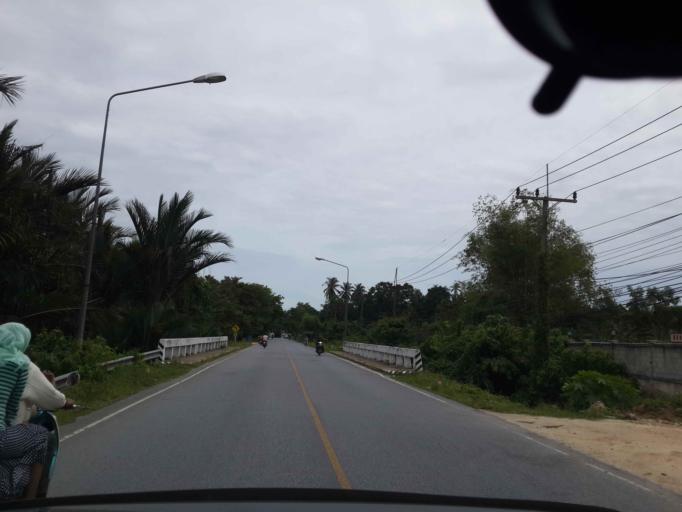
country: TH
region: Narathiwat
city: Yi-ngo
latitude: 6.3455
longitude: 101.6602
